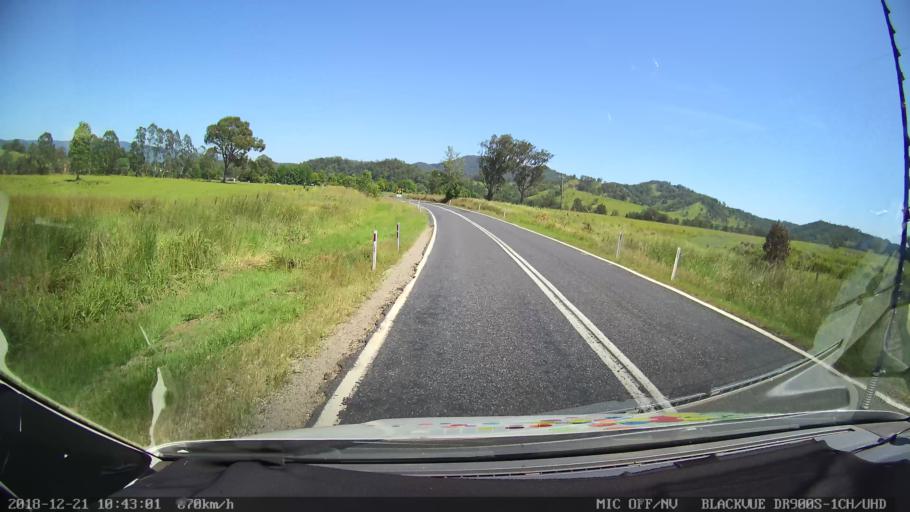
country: AU
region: New South Wales
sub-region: Clarence Valley
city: Gordon
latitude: -29.5796
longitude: 152.5600
